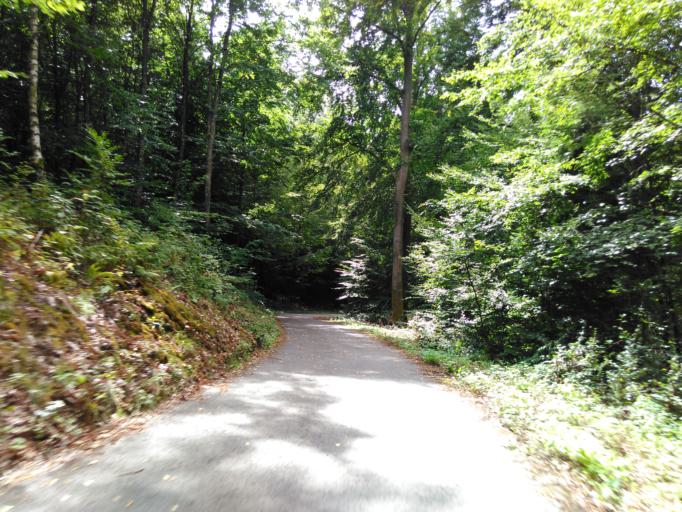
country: LU
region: Grevenmacher
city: Gonderange
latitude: 49.6700
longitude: 6.2278
